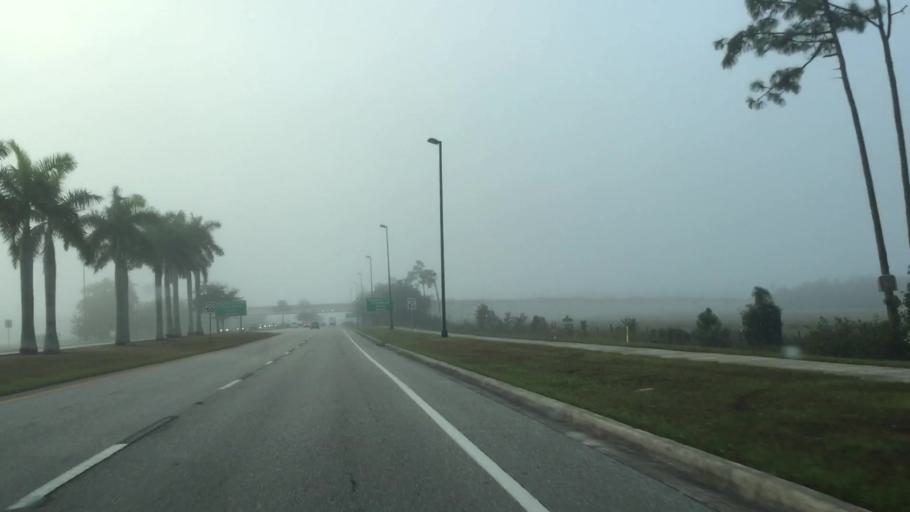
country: US
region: Florida
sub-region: Lee County
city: Three Oaks
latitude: 26.5151
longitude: -81.7857
